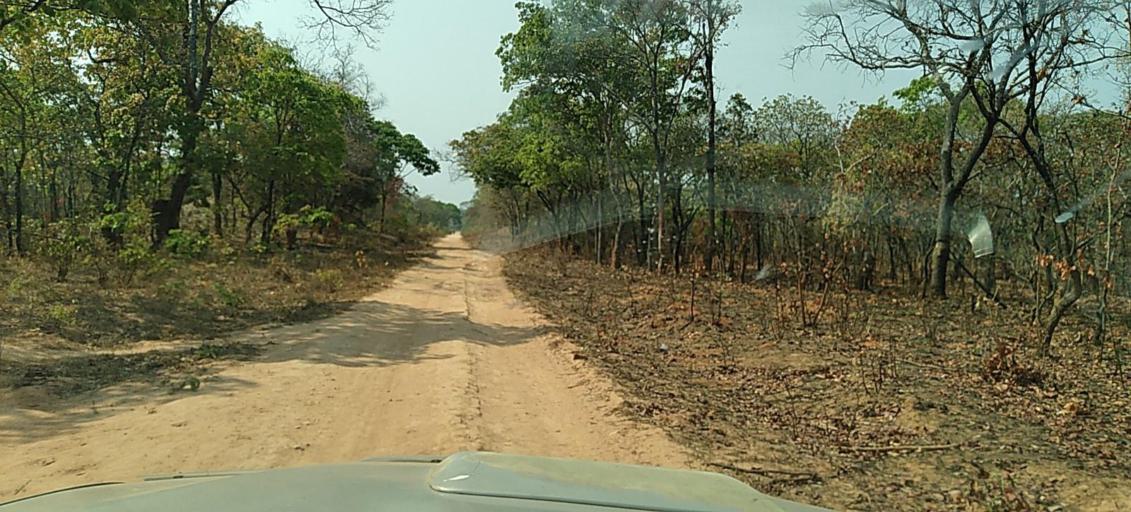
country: ZM
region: North-Western
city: Kasempa
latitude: -13.5466
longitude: 26.4087
